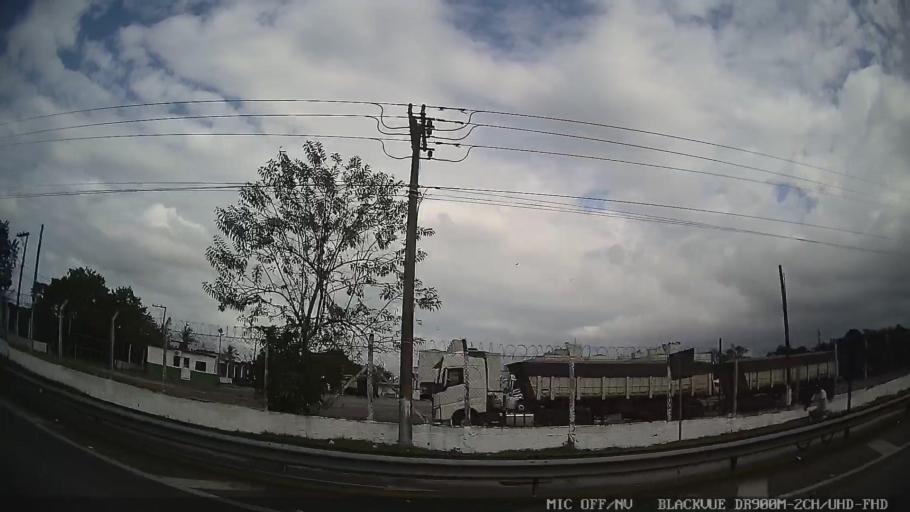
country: BR
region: Sao Paulo
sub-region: Guaruja
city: Guaruja
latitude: -23.9732
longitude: -46.2690
